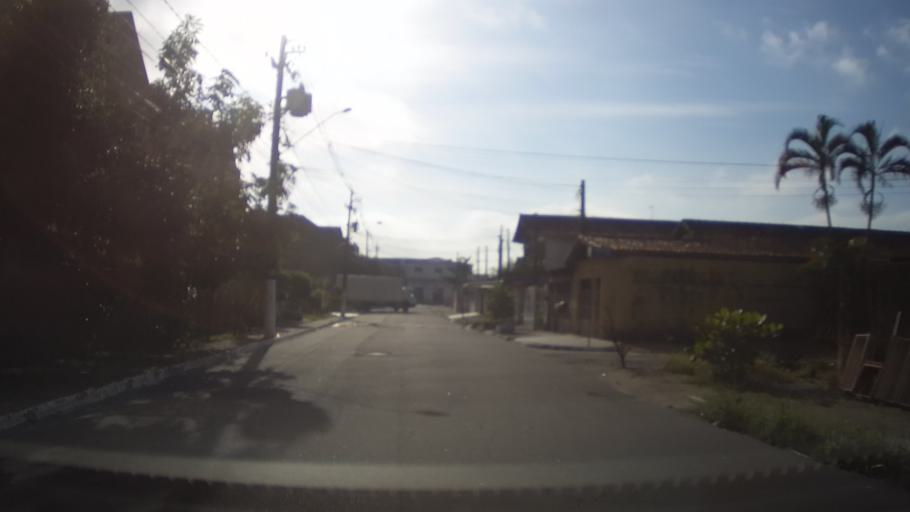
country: BR
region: Sao Paulo
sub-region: Praia Grande
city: Praia Grande
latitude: -24.0170
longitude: -46.4800
